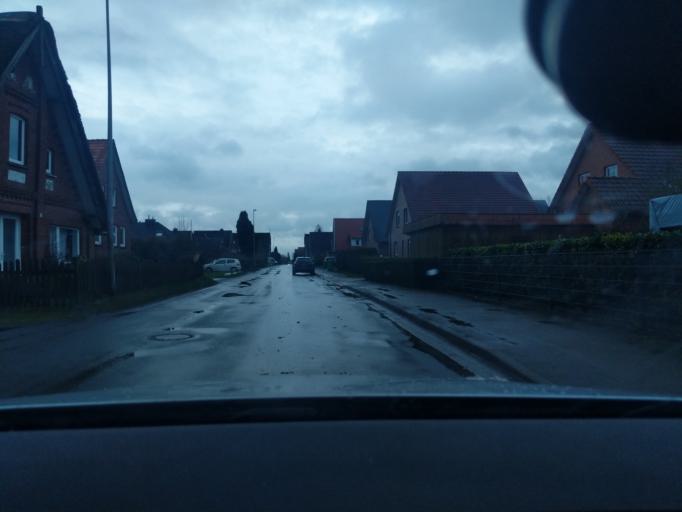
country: DE
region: Lower Saxony
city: Jork
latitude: 53.5212
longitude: 9.6599
